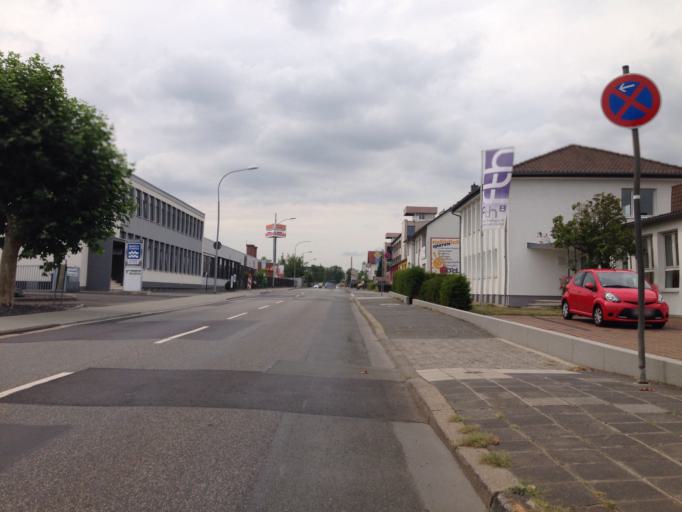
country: DE
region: Hesse
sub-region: Regierungsbezirk Giessen
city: Giessen
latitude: 50.5730
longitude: 8.6935
